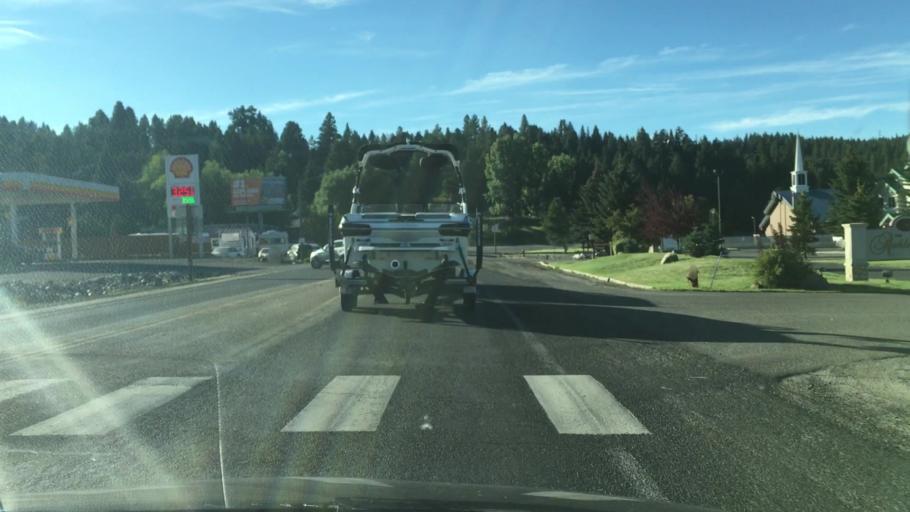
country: US
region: Idaho
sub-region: Valley County
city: Cascade
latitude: 44.5192
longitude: -116.0448
